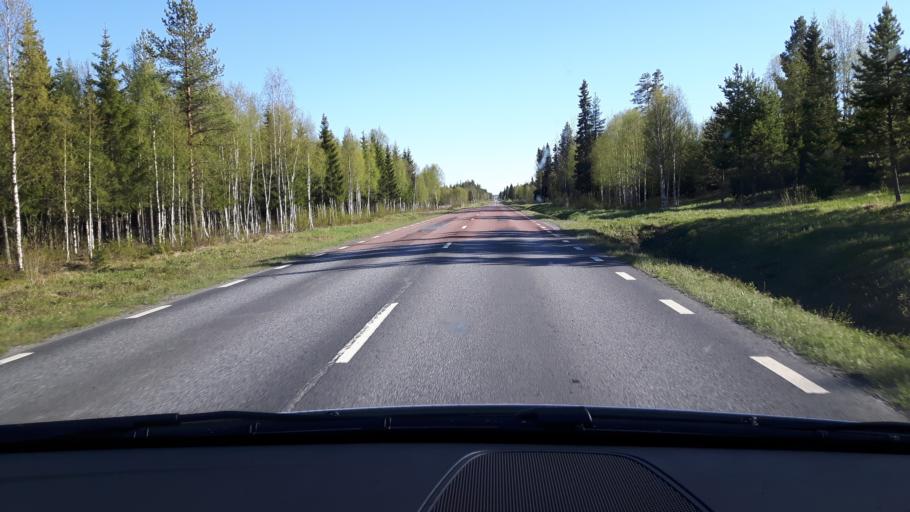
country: SE
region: Jaemtland
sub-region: Stroemsunds Kommun
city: Stroemsund
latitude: 63.7999
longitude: 15.5166
